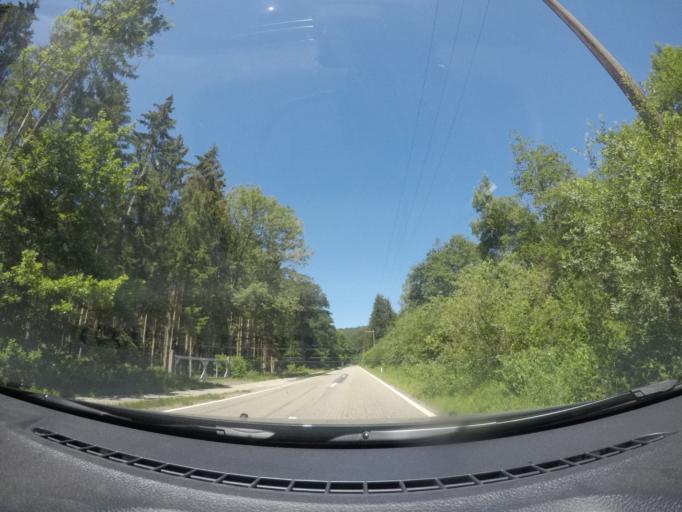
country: BE
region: Wallonia
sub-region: Province du Luxembourg
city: Wellin
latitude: 50.0552
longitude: 5.1407
